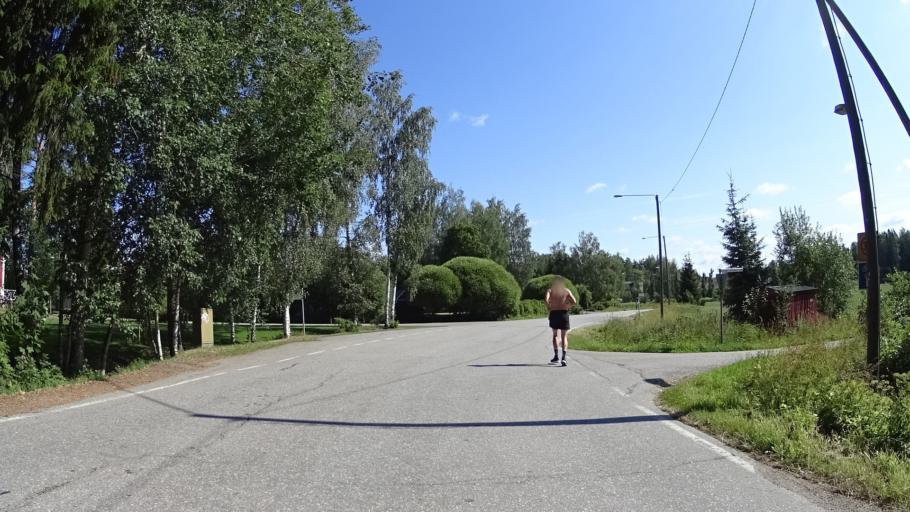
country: FI
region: Uusimaa
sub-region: Helsinki
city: Tuusula
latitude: 60.4286
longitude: 25.0495
